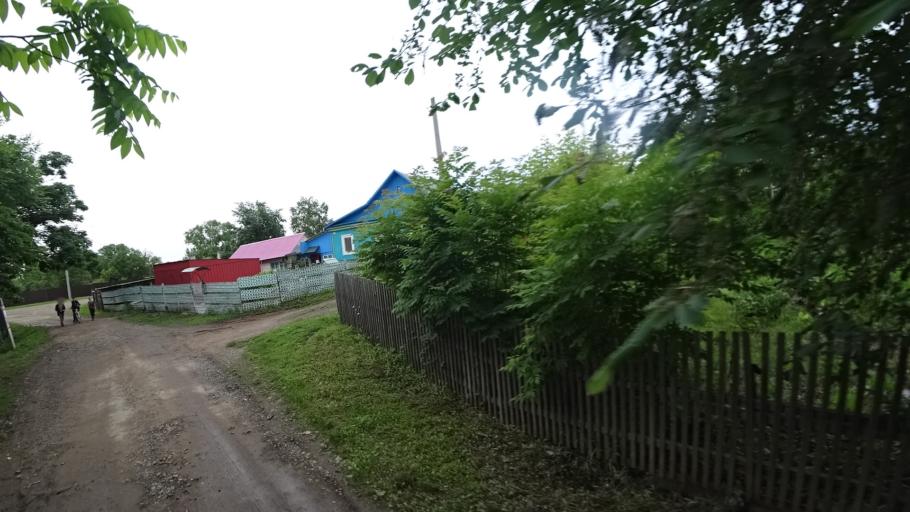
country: RU
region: Primorskiy
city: Novosysoyevka
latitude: 44.2258
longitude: 133.3543
